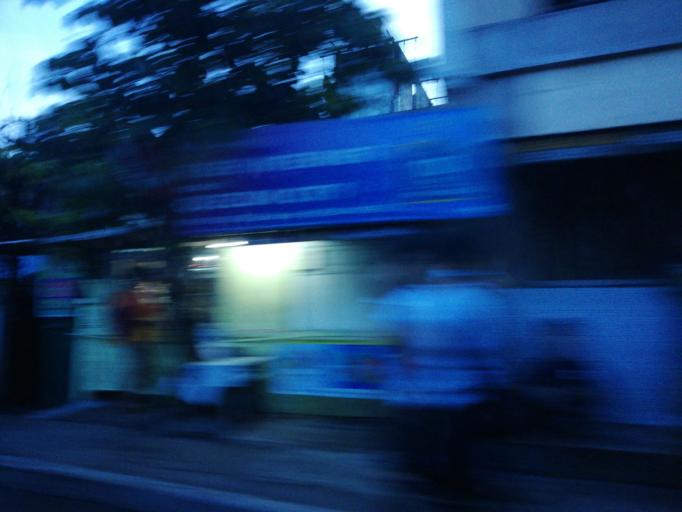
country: PH
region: Calabarzon
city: Bagong Pagasa
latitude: 14.6610
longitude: 121.0350
